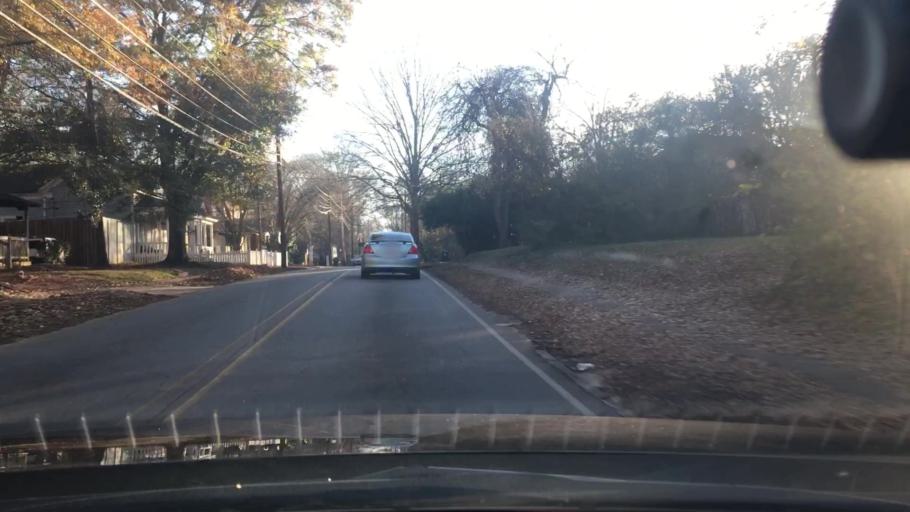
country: US
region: Georgia
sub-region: Spalding County
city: Griffin
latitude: 33.2460
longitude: -84.2744
